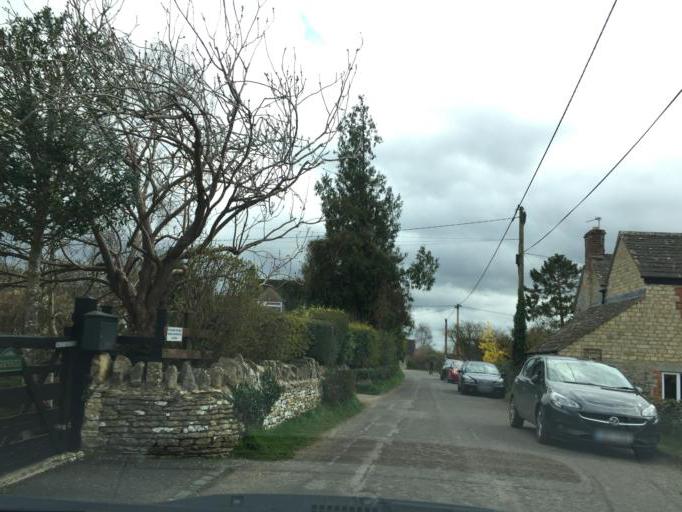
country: GB
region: England
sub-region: Oxfordshire
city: Stonesfield
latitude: 51.8502
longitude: -1.4305
